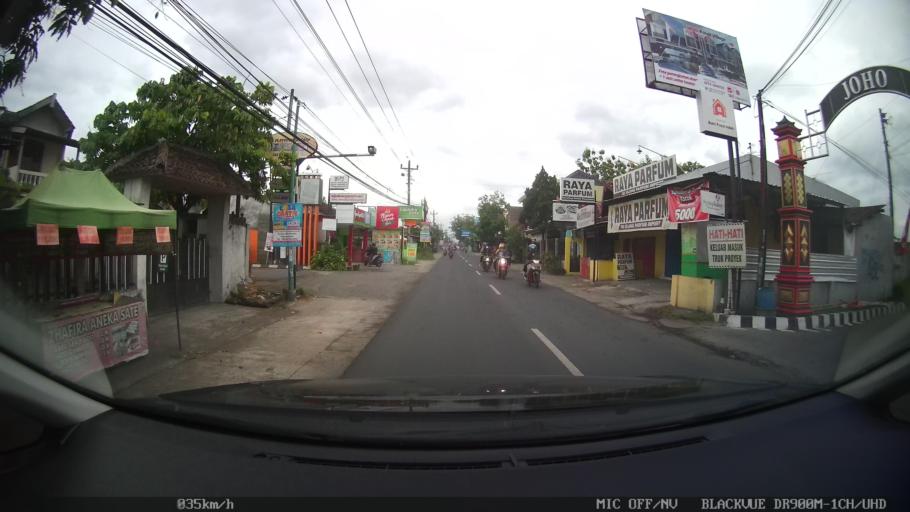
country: ID
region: Daerah Istimewa Yogyakarta
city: Sewon
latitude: -7.8464
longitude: 110.4107
